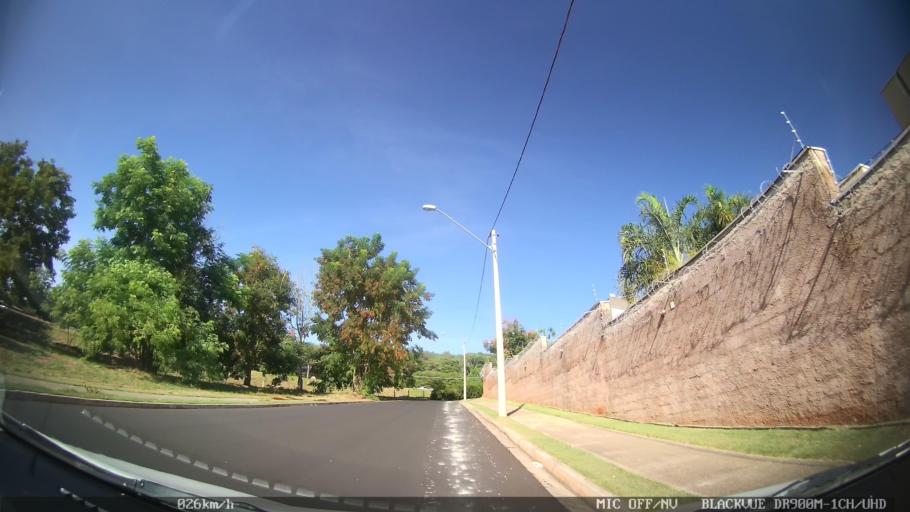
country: BR
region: Sao Paulo
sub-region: Ribeirao Preto
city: Ribeirao Preto
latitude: -21.2211
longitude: -47.7906
